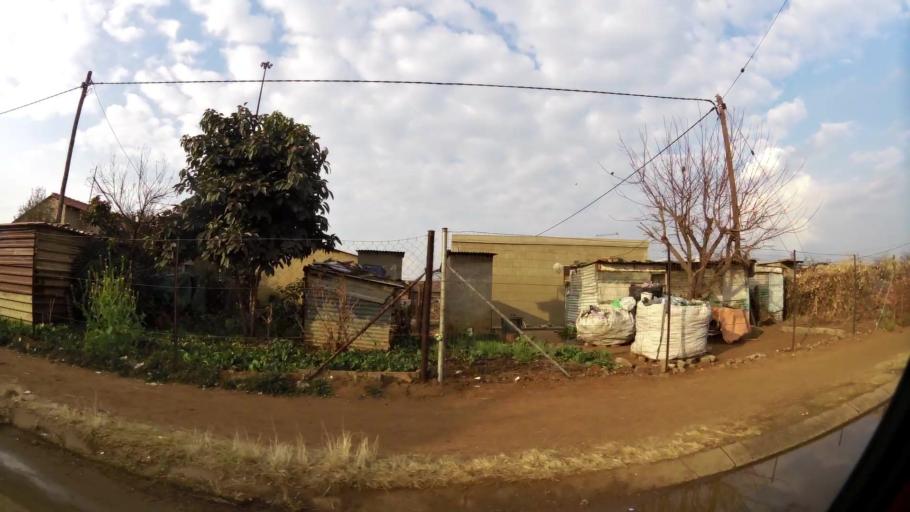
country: ZA
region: Gauteng
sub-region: Sedibeng District Municipality
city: Vanderbijlpark
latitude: -26.6787
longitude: 27.8693
